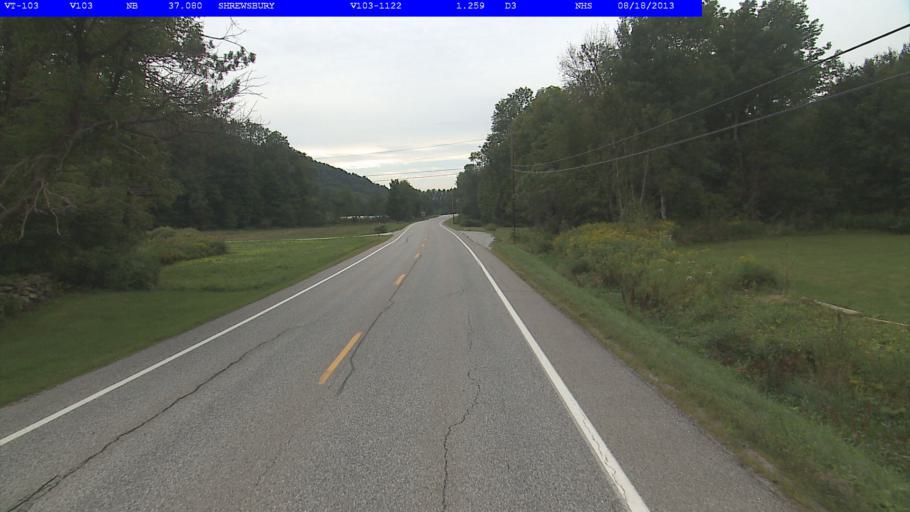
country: US
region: Vermont
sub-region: Rutland County
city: Rutland
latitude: 43.4939
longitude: -72.8898
